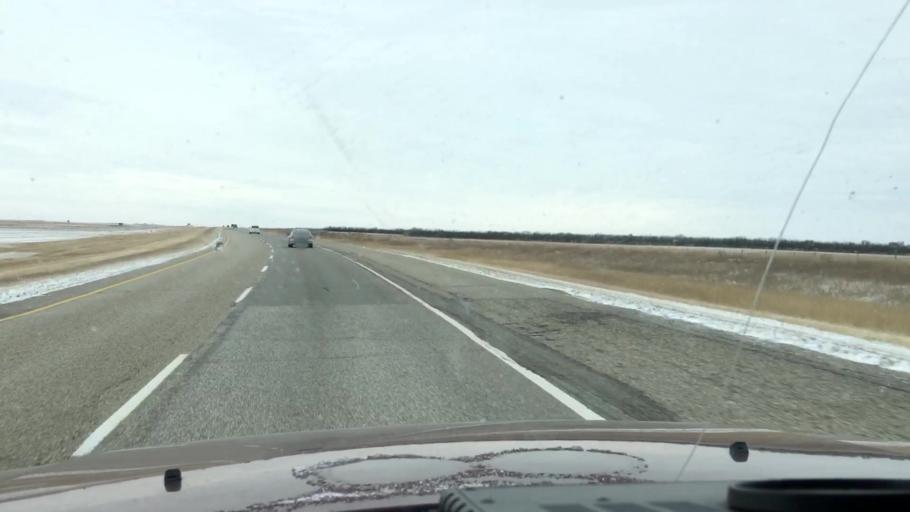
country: CA
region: Saskatchewan
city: Saskatoon
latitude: 51.4704
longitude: -106.2467
